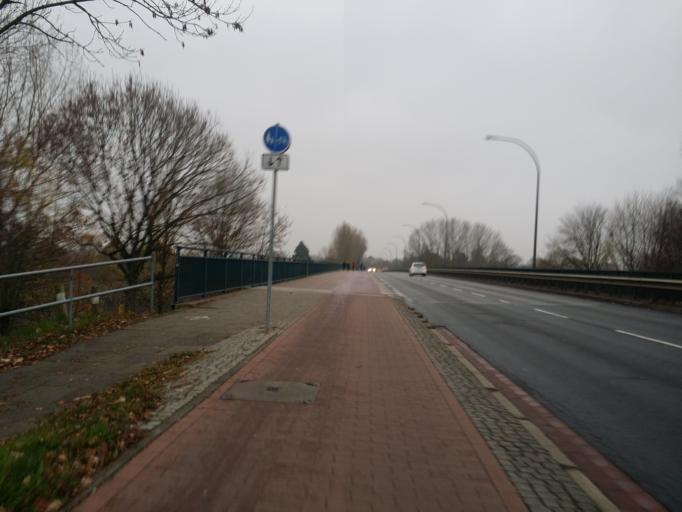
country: DE
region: Bremen
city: Bremen
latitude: 53.0607
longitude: 8.8527
